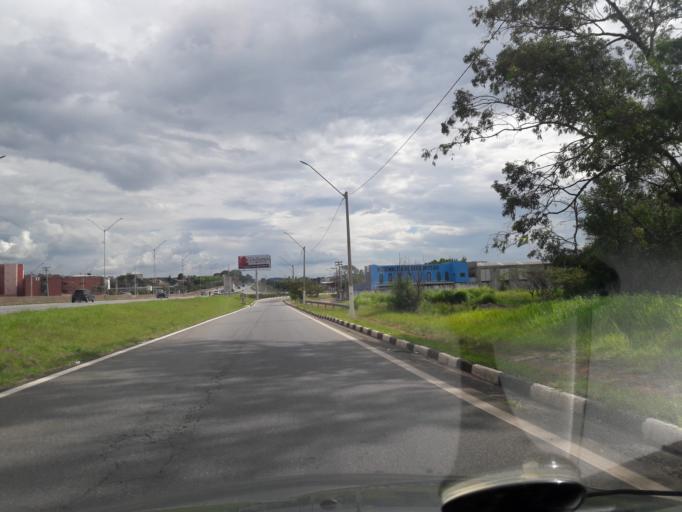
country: BR
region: Sao Paulo
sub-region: Atibaia
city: Atibaia
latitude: -23.1117
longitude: -46.5713
